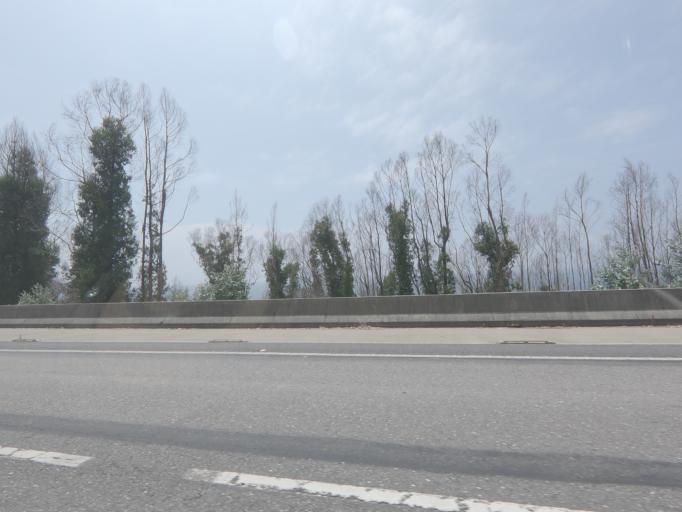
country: ES
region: Galicia
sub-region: Provincia de Pontevedra
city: A Guarda
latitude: 41.9327
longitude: -8.8829
